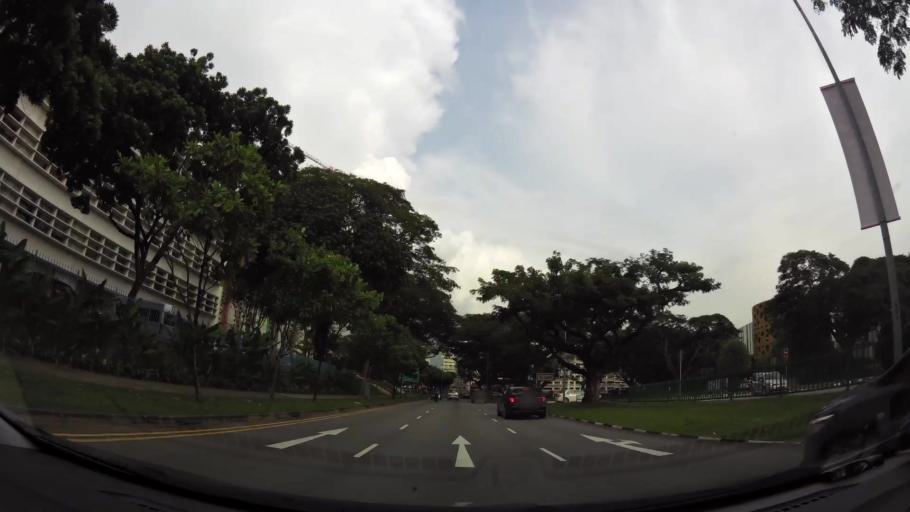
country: SG
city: Singapore
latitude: 1.3315
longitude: 103.8534
